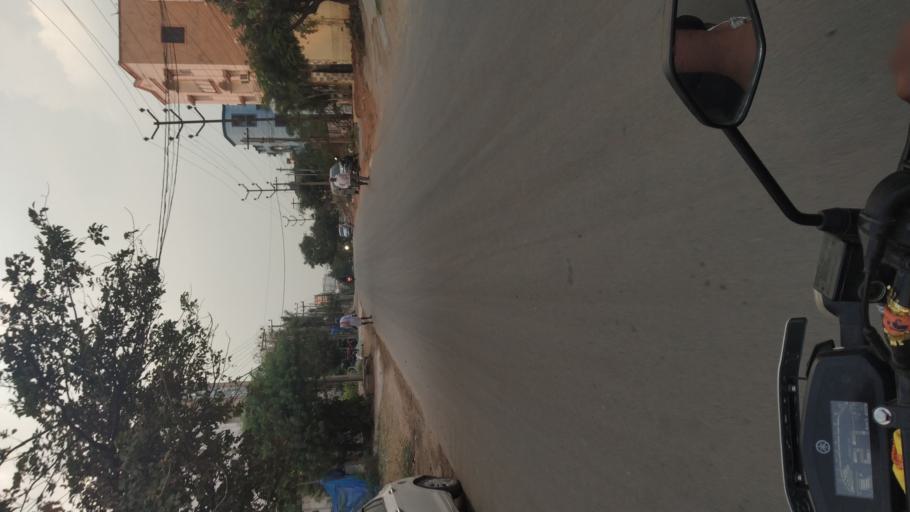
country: IN
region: Telangana
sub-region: Medak
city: Serilingampalle
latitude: 17.4897
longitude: 78.3277
